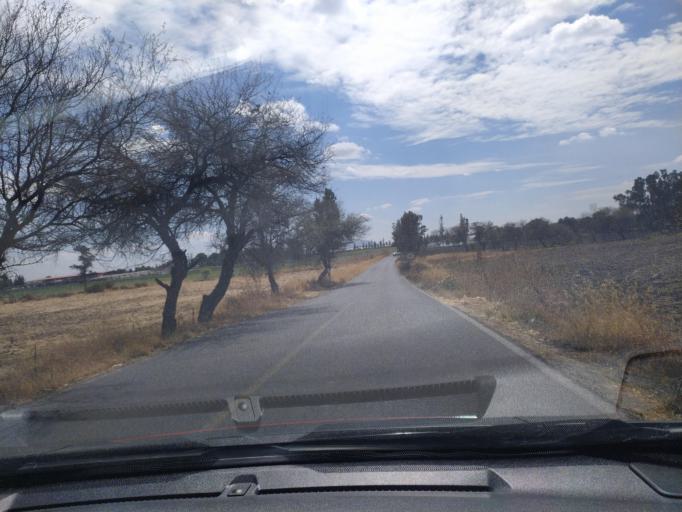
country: MX
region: Guanajuato
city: San Roque
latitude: 20.9700
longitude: -101.8293
